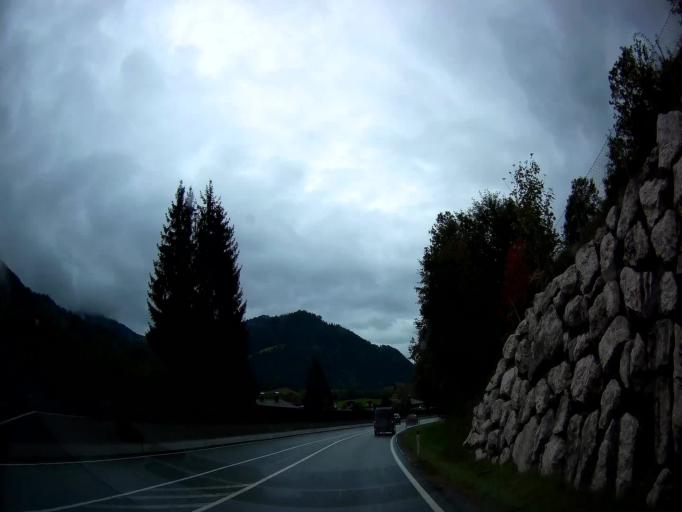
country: AT
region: Tyrol
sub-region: Politischer Bezirk Kufstein
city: Soll
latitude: 47.5076
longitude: 12.2074
